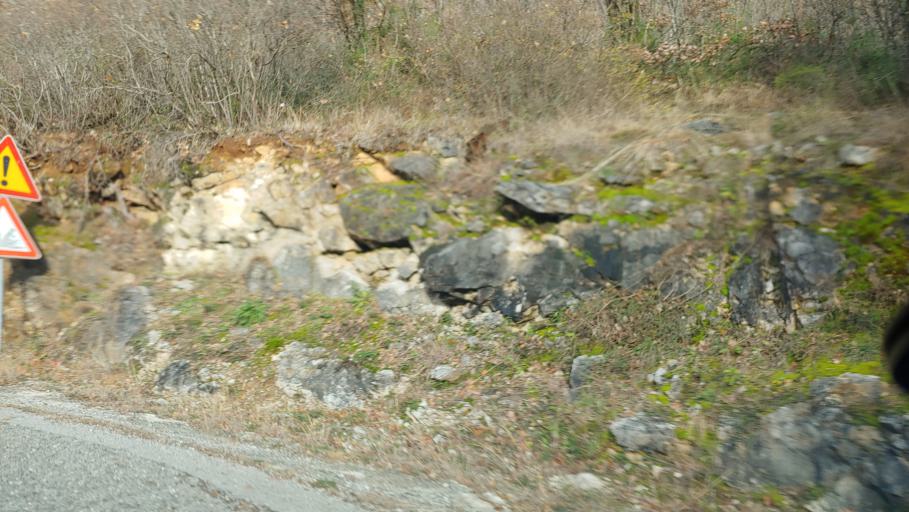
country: IT
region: Friuli Venezia Giulia
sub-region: Provincia di Trieste
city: Sistiana-Visogliano
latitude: 45.8162
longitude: 13.6278
